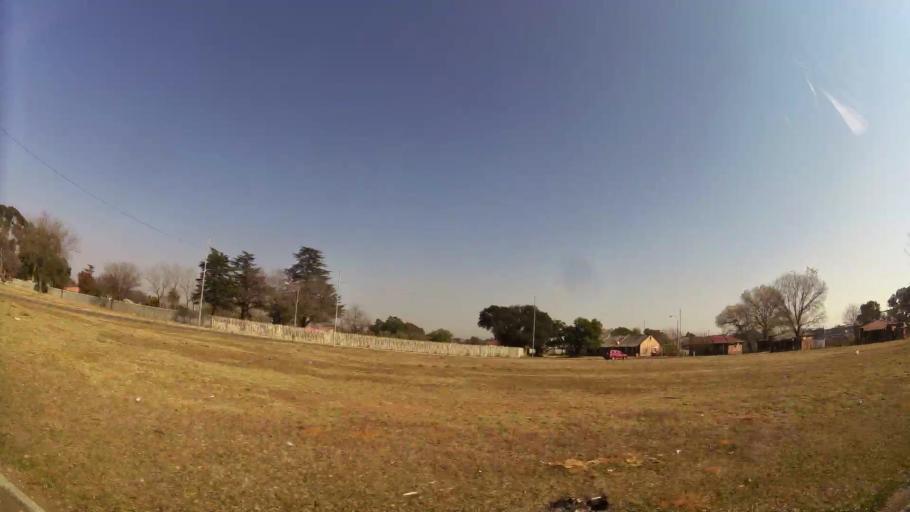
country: ZA
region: Gauteng
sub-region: Ekurhuleni Metropolitan Municipality
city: Boksburg
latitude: -26.2187
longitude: 28.2637
